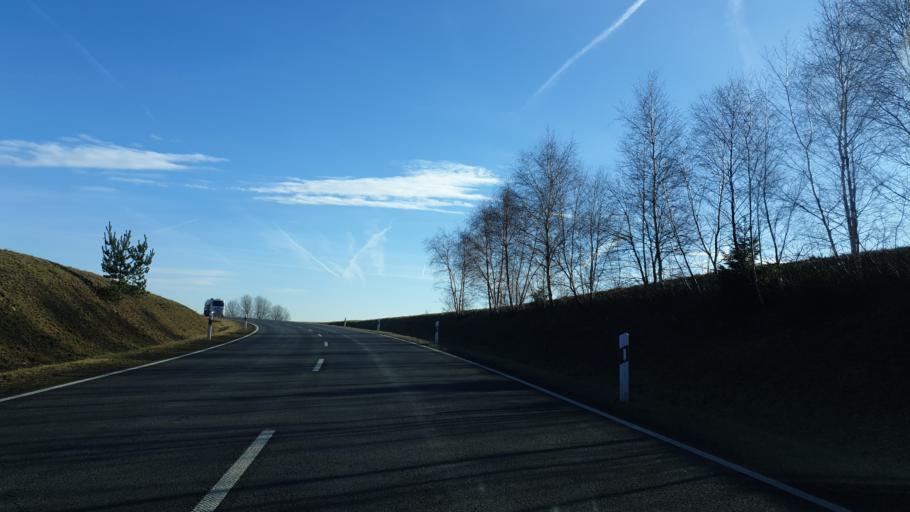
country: DE
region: Saxony
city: Bad Brambach
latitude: 50.2314
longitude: 12.3090
